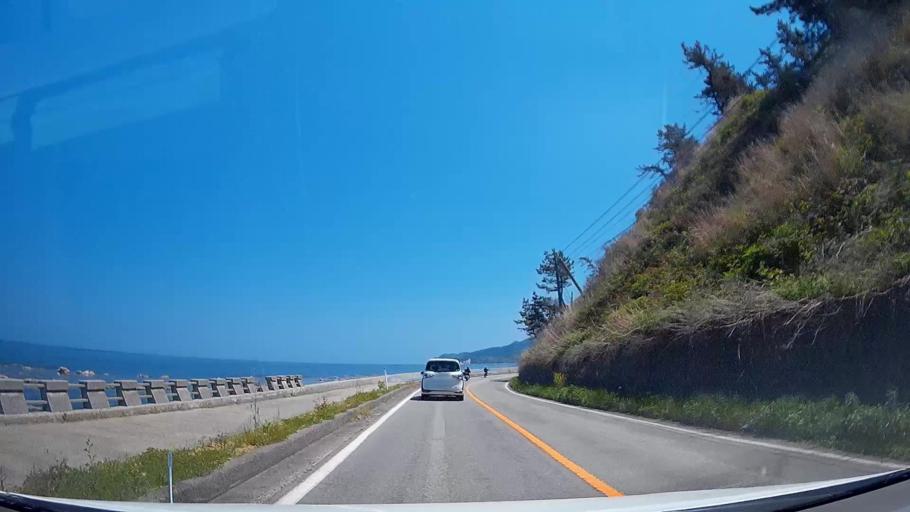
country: JP
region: Ishikawa
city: Nanao
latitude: 37.4301
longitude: 137.0087
